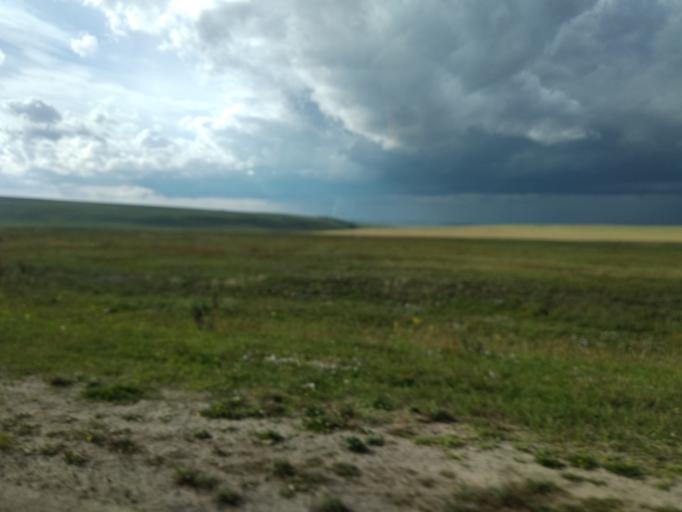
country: RU
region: Irkutsk
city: Bayanday
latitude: 52.9789
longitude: 105.3977
